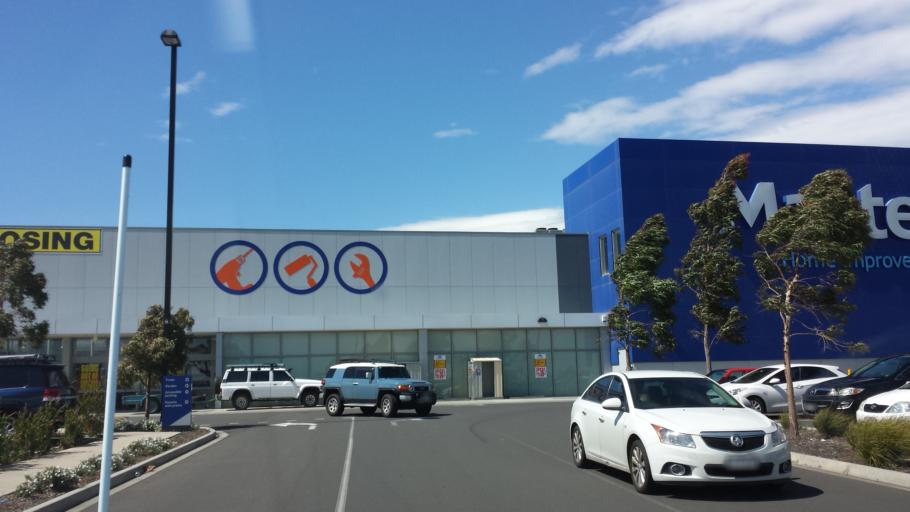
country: AU
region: Victoria
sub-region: Casey
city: Eumemmerring
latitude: -38.0043
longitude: 145.2497
